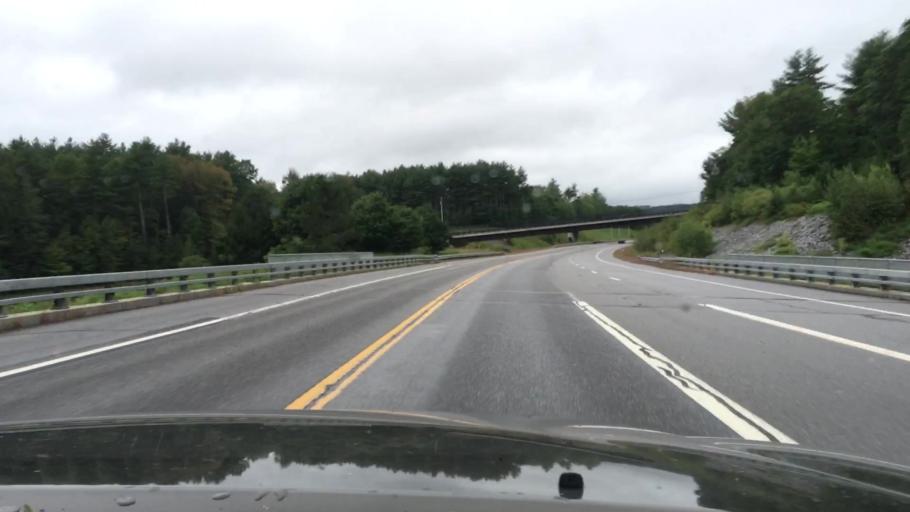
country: US
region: New Hampshire
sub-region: Hillsborough County
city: Hillsborough
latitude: 43.1164
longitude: -71.9175
